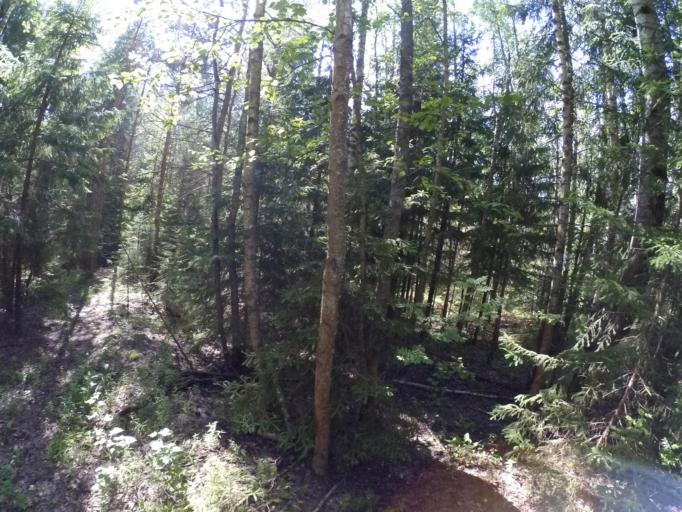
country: RU
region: Moskovskaya
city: Fosforitnyy
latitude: 55.3333
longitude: 38.9420
